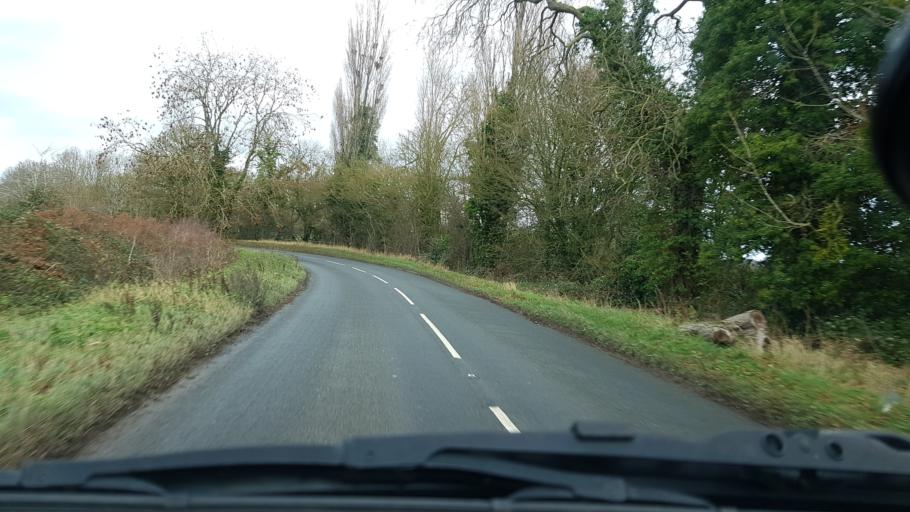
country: GB
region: England
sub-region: Worcestershire
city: Bredon
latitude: 52.0115
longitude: -2.0894
